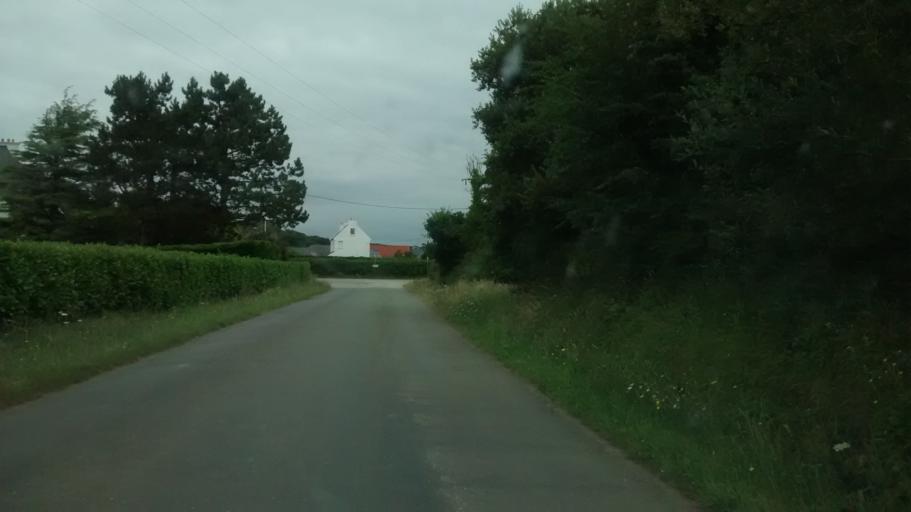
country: FR
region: Brittany
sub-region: Departement du Finistere
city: Plougastel-Daoulas
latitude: 48.3345
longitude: -4.3915
